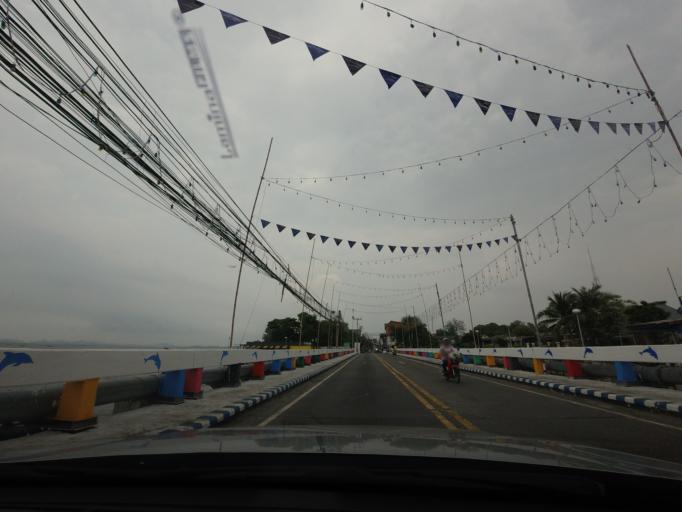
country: TH
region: Chon Buri
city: Phatthaya
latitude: 12.9761
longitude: 100.9090
